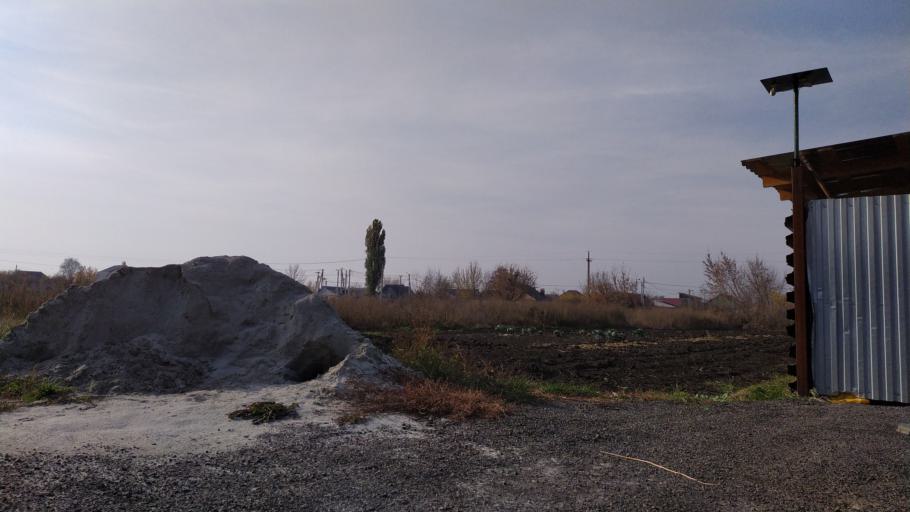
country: RU
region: Kursk
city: Kursk
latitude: 51.6411
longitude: 36.1506
